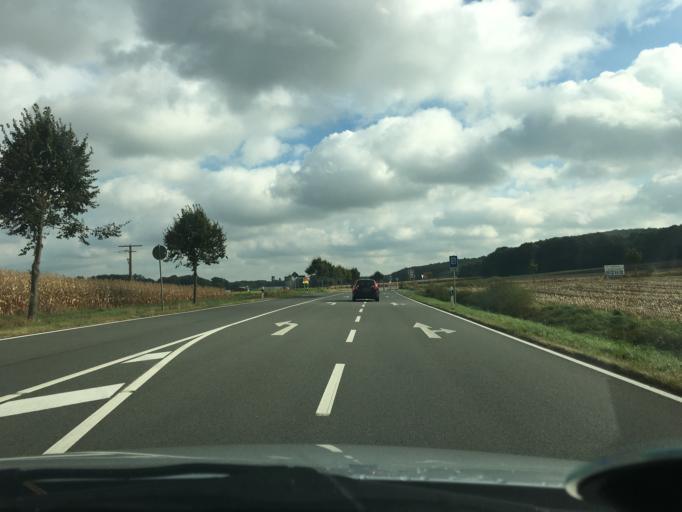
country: DE
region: Lower Saxony
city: Wallenhorst
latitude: 52.4026
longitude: 8.0926
